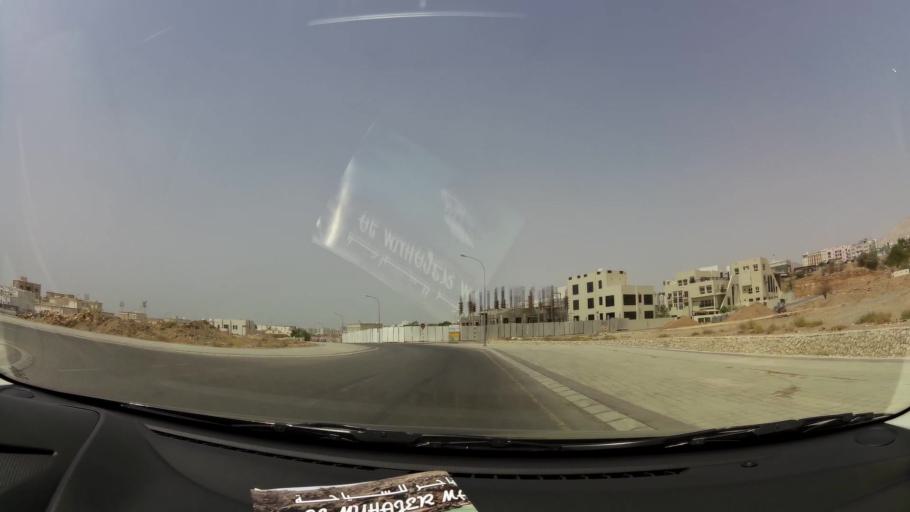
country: OM
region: Muhafazat Masqat
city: Bawshar
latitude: 23.5632
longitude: 58.3990
